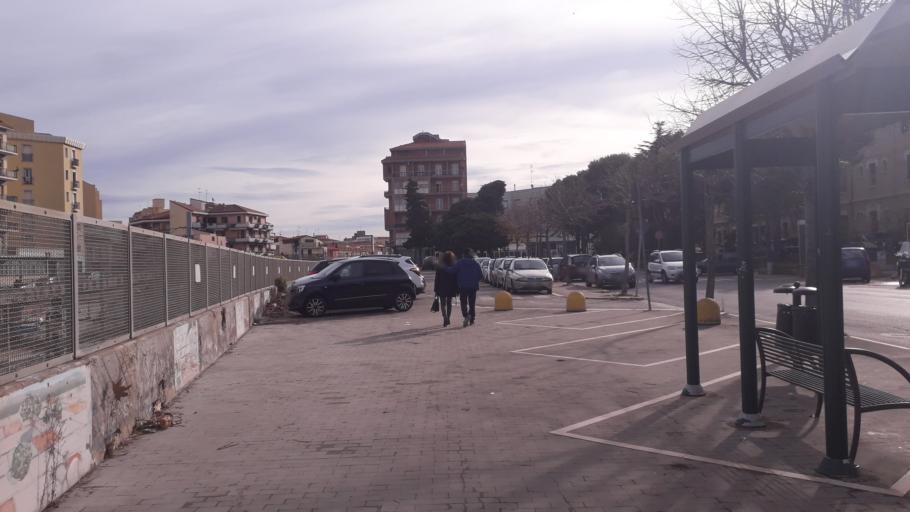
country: IT
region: Molise
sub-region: Provincia di Campobasso
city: Termoli
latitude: 41.9994
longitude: 14.9936
